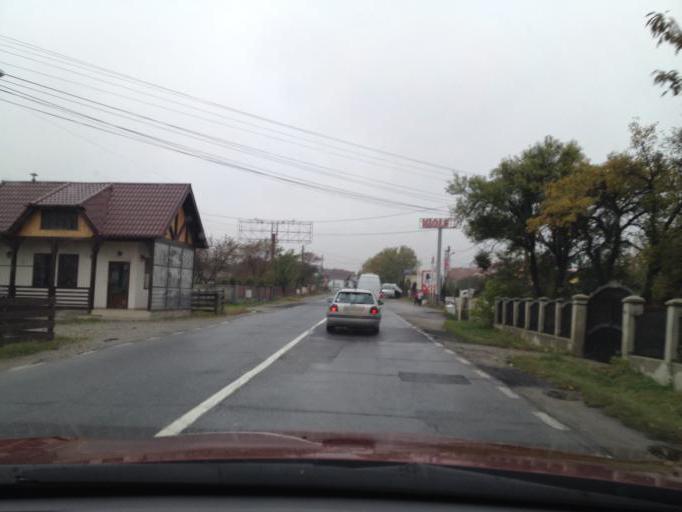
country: RO
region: Brasov
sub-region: Comuna Zarnesti
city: Tohanu Nou
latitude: 45.5327
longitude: 25.3742
